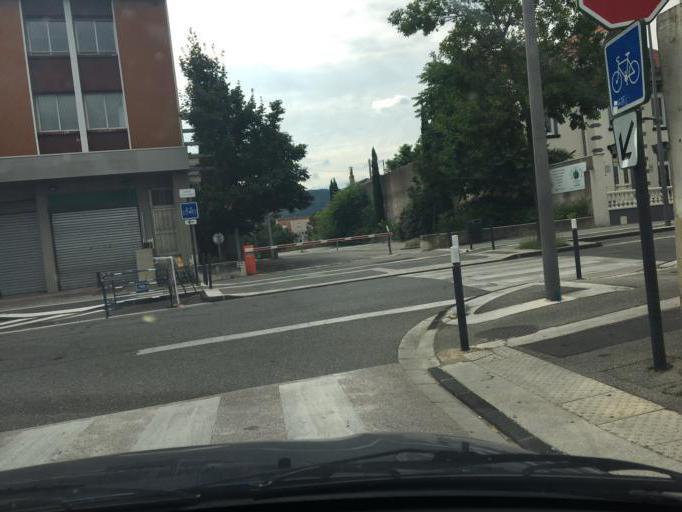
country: FR
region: Rhone-Alpes
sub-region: Departement de l'Ardeche
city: Guilherand-Granges
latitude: 44.9178
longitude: 4.8856
